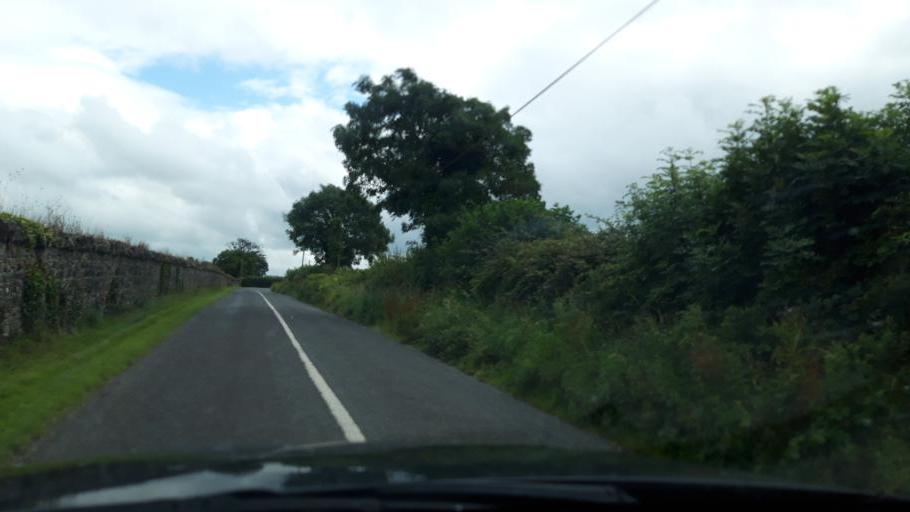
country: IE
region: Munster
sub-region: County Cork
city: Castlemartyr
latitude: 52.1353
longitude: -8.0142
